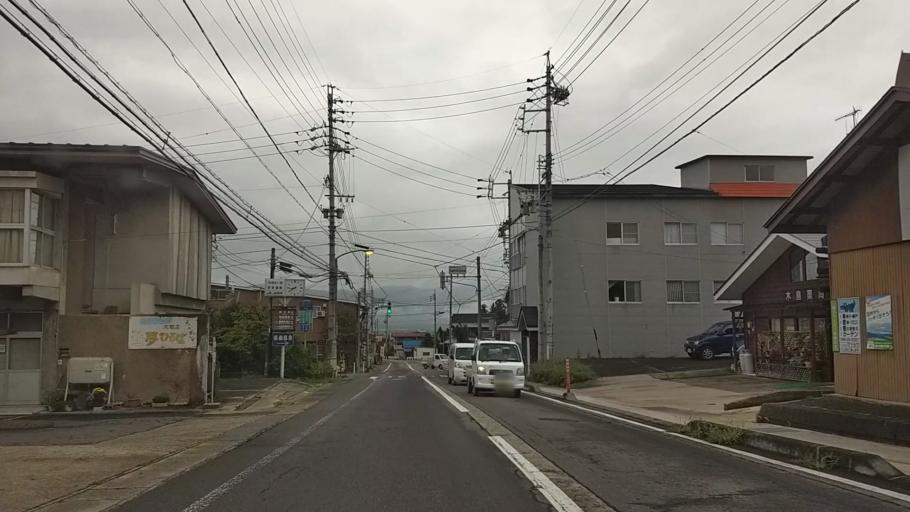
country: JP
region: Nagano
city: Iiyama
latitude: 36.8388
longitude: 138.4081
